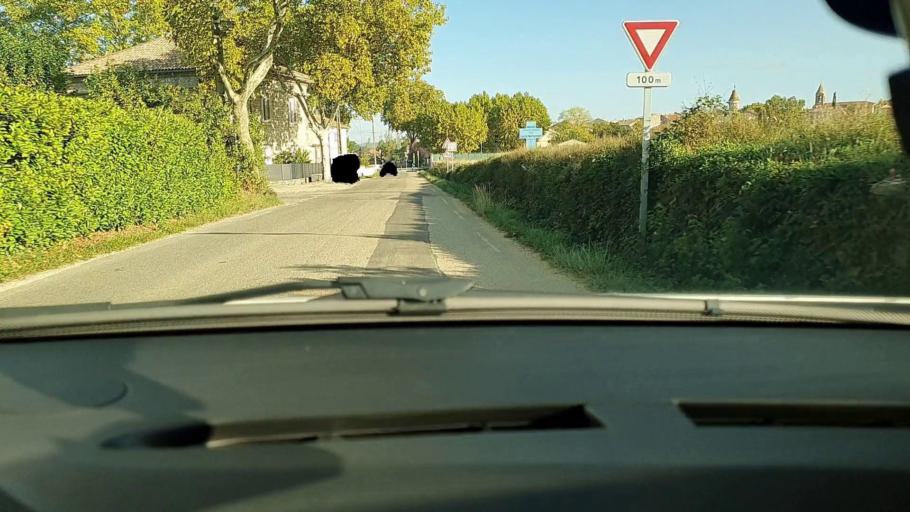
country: FR
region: Languedoc-Roussillon
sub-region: Departement du Gard
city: Barjac
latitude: 44.2532
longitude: 4.2918
